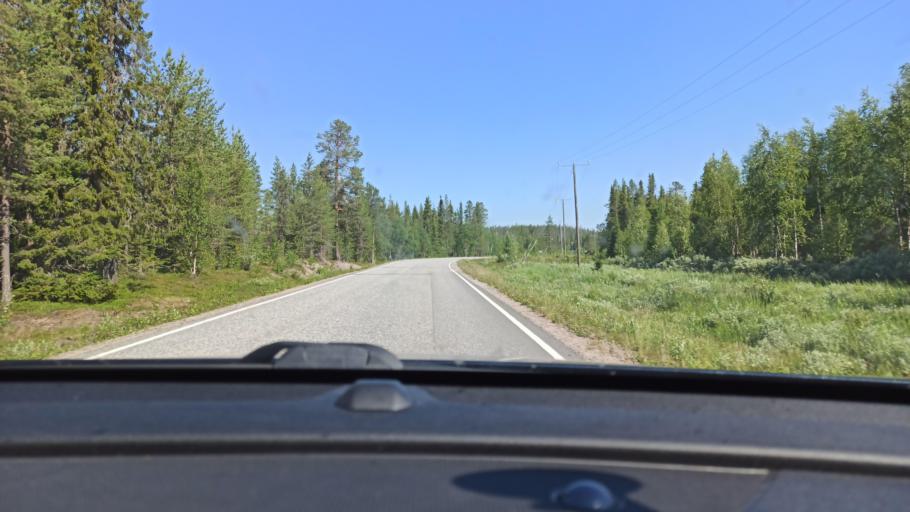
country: FI
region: Lapland
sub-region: Tunturi-Lappi
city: Kolari
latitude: 67.6292
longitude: 24.1562
